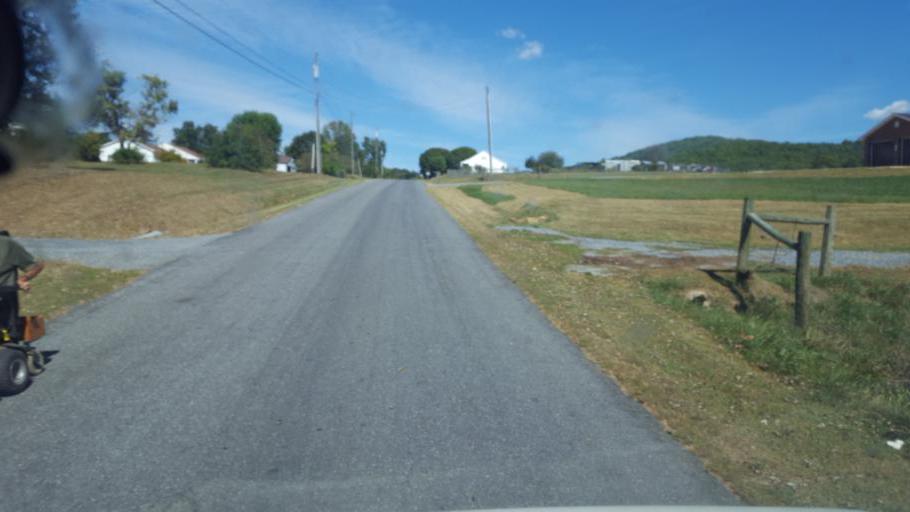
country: US
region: Virginia
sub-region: Rockingham County
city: Elkton
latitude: 38.3896
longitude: -78.5772
